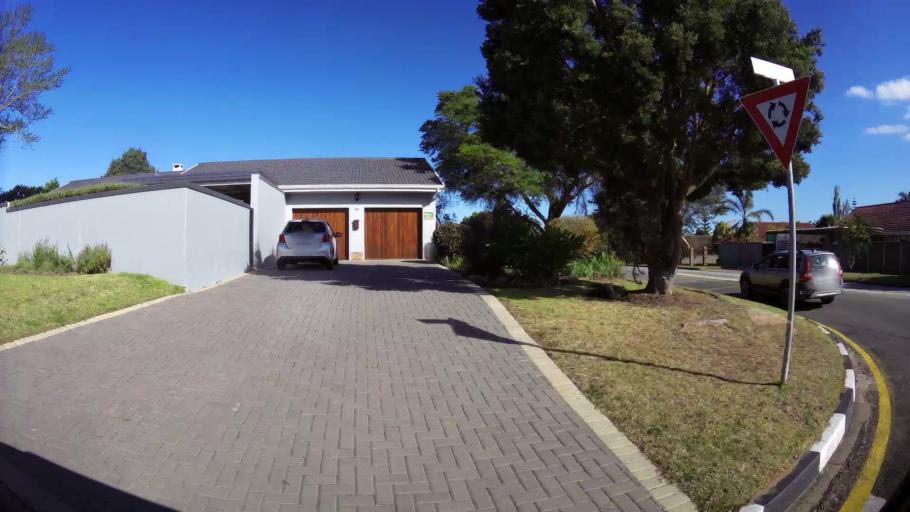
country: ZA
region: Western Cape
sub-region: Eden District Municipality
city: George
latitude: -33.9644
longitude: 22.4923
